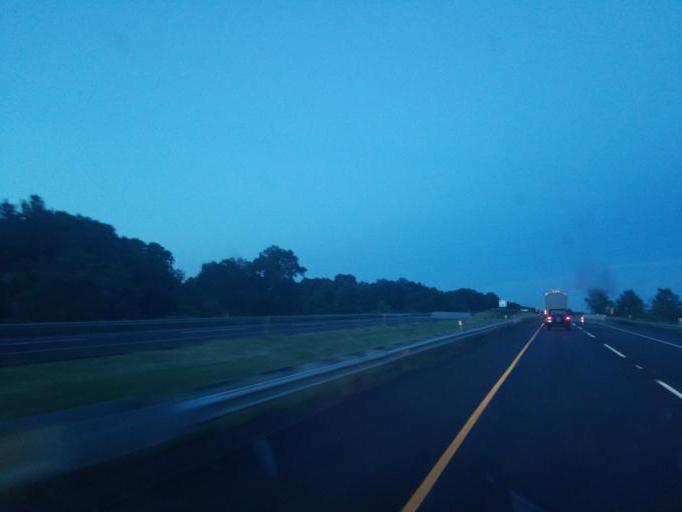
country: US
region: Indiana
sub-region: Saint Joseph County
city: Granger
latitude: 41.7336
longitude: -86.1318
